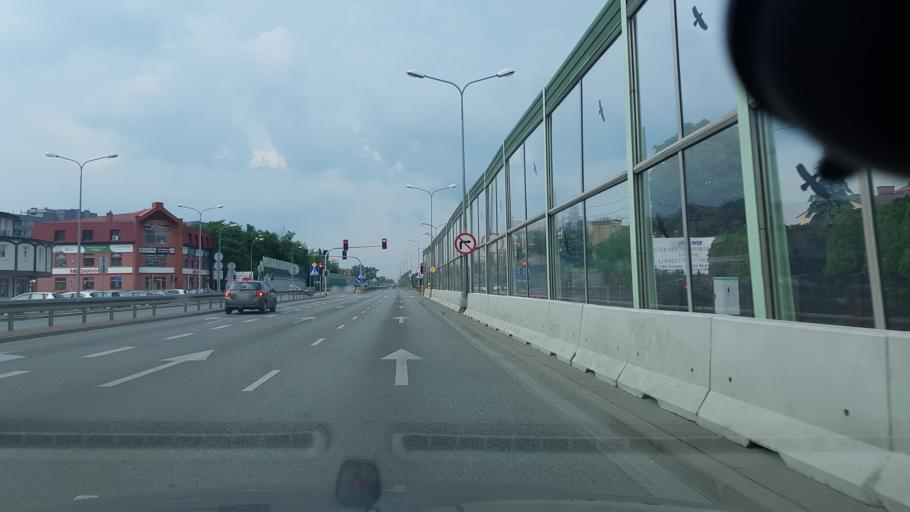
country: PL
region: Masovian Voivodeship
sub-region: Powiat legionowski
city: Legionowo
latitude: 52.3918
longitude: 20.9341
